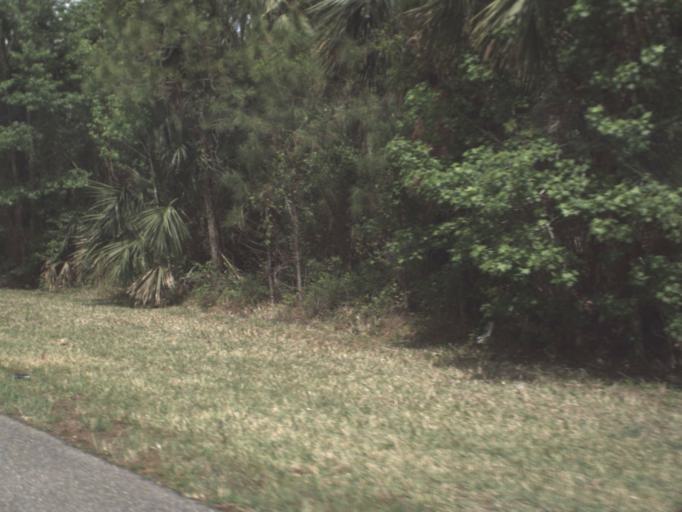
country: US
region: Florida
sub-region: Flagler County
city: Bunnell
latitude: 29.3773
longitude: -81.3108
